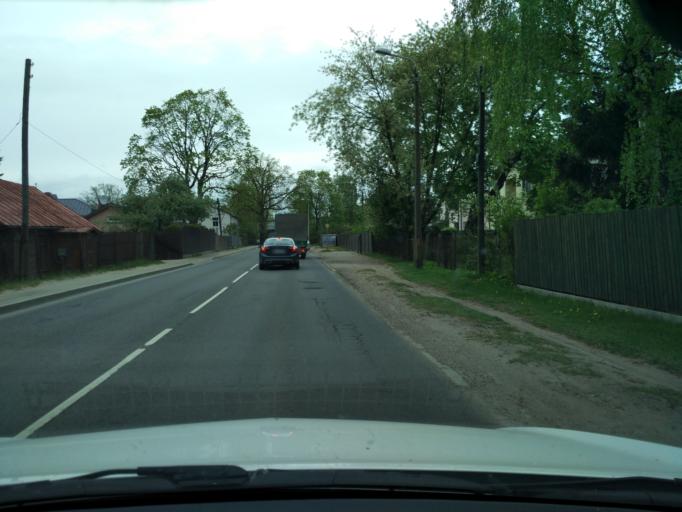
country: LV
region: Marupe
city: Marupe
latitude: 56.9198
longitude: 24.0759
